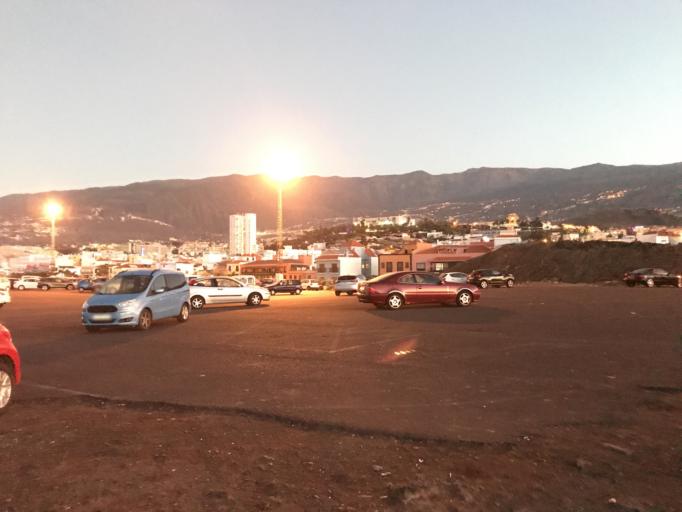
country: ES
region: Canary Islands
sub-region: Provincia de Santa Cruz de Tenerife
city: Puerto de la Cruz
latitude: 28.4184
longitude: -16.5553
